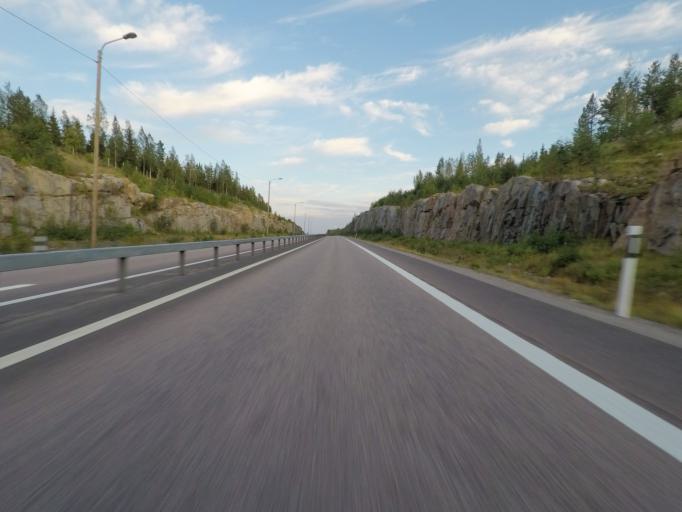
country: FI
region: Central Finland
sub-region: Jyvaeskylae
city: Toivakka
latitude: 62.0991
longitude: 25.9876
